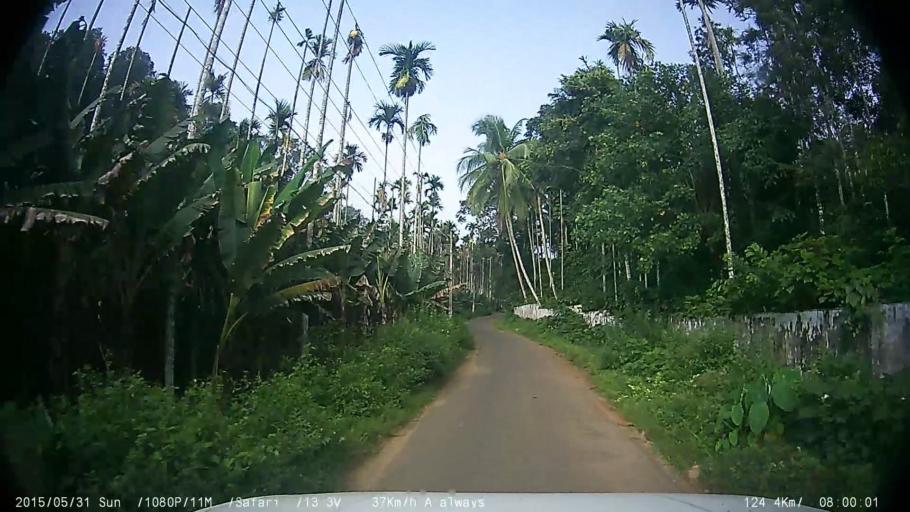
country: IN
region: Kerala
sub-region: Wayanad
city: Kalpetta
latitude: 11.6333
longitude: 76.0538
